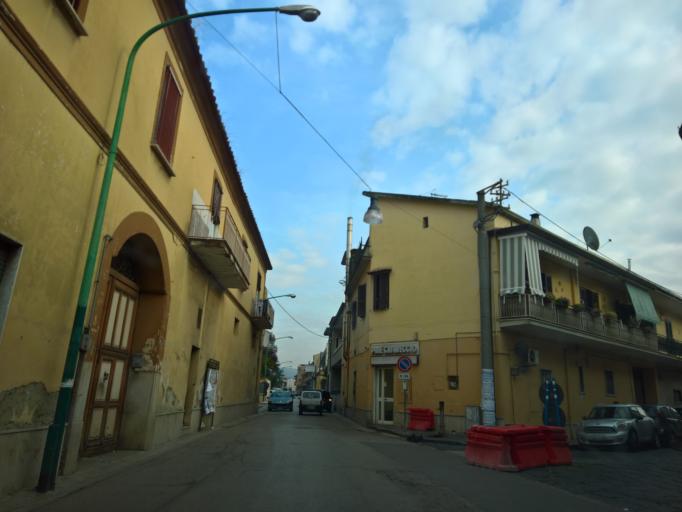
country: IT
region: Campania
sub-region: Provincia di Caserta
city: San Prisco
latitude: 41.0879
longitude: 14.2751
